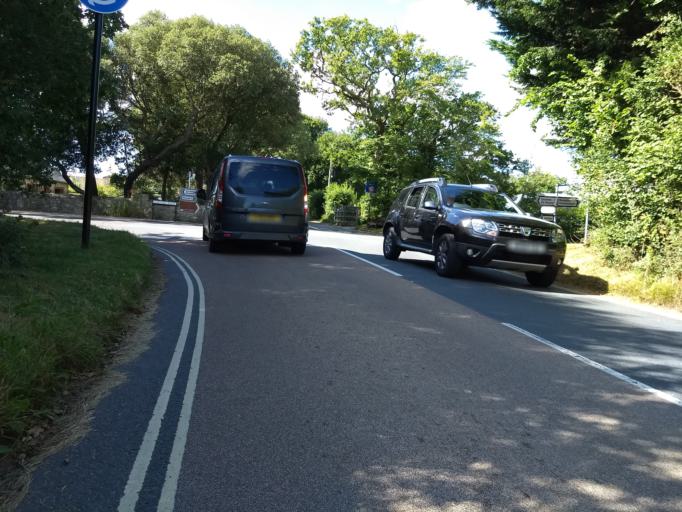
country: GB
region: England
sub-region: Isle of Wight
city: Ryde
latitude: 50.7106
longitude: -1.1785
